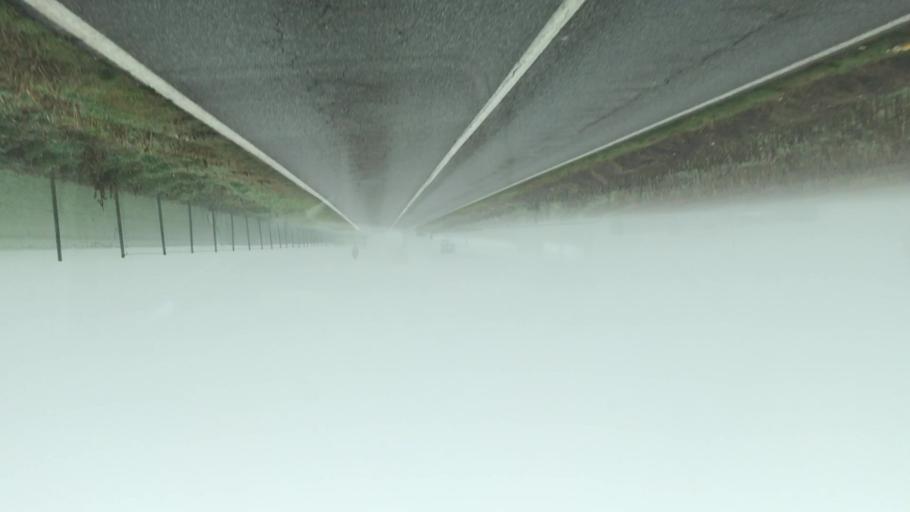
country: IT
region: Lombardy
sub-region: Provincia di Brescia
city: Novagli
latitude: 45.3817
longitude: 10.4104
